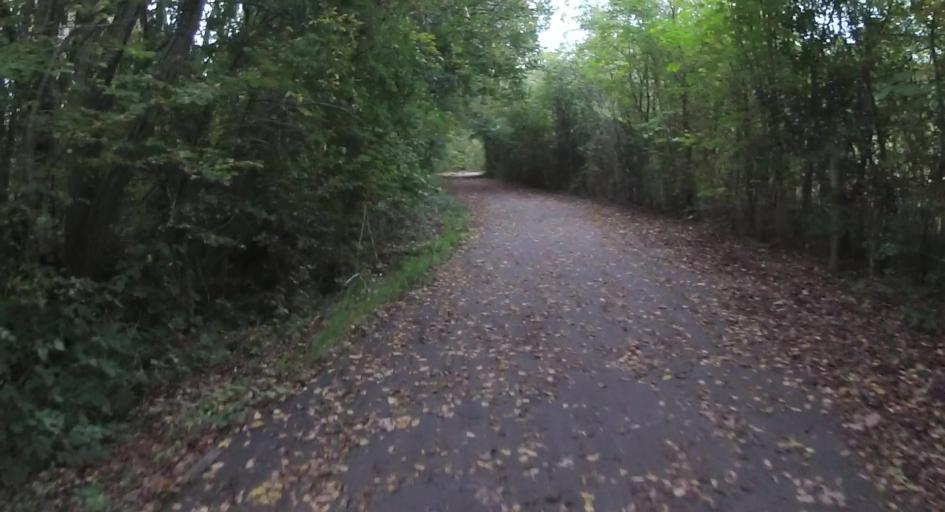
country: GB
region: England
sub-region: Bracknell Forest
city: Binfield
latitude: 51.4055
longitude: -0.7873
